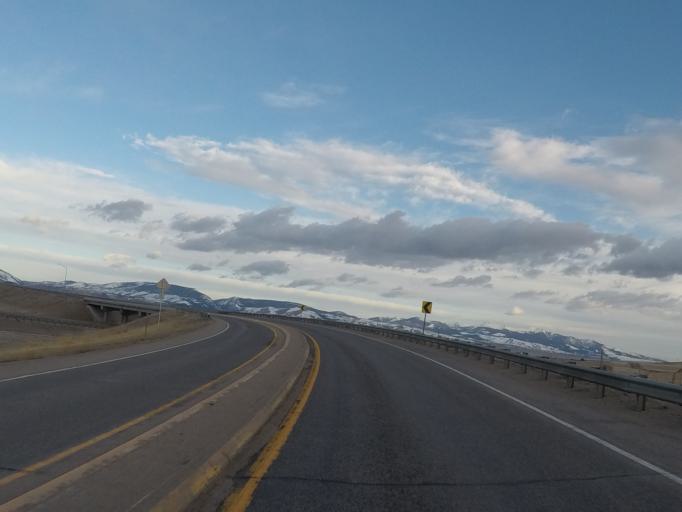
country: US
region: Montana
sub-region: Deer Lodge County
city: Warm Springs
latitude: 46.0946
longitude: -112.7907
